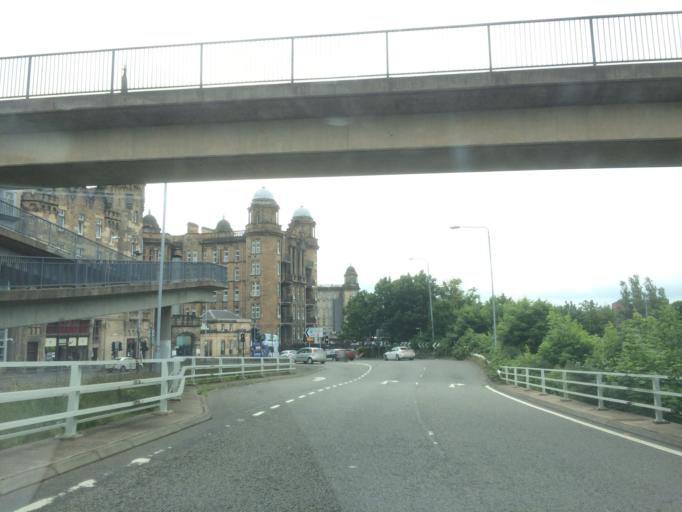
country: GB
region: Scotland
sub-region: Glasgow City
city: Glasgow
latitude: 55.8657
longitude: -4.2362
